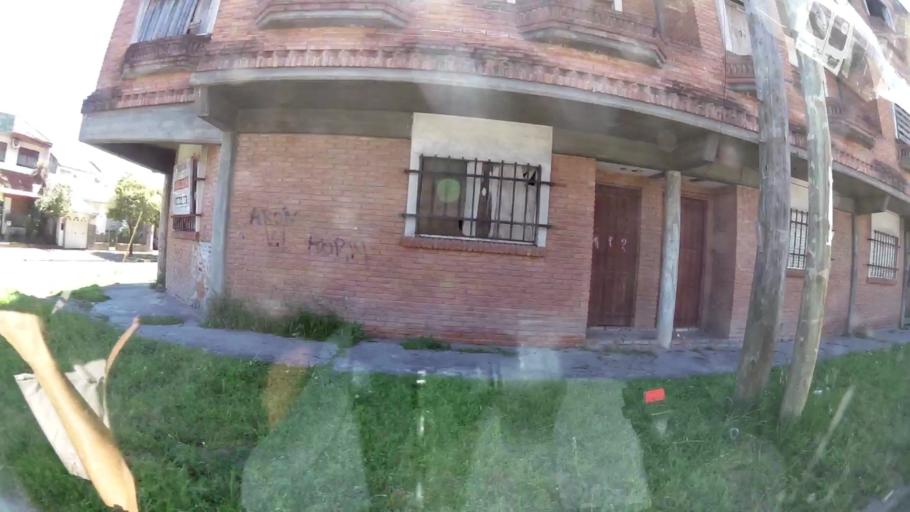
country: AR
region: Buenos Aires
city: Caseros
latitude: -34.5753
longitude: -58.5631
